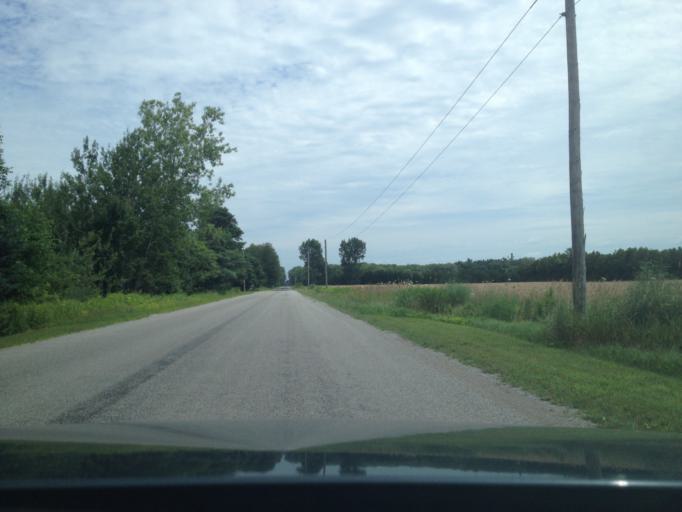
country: CA
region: Ontario
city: Norfolk County
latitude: 42.8537
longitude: -80.4098
